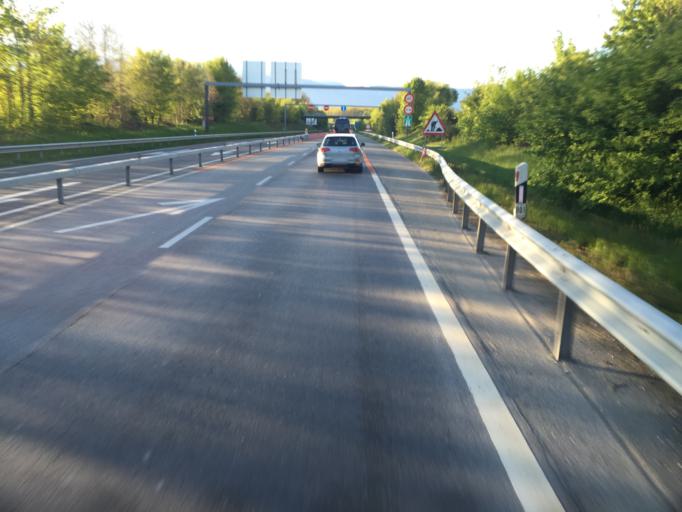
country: CH
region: Geneva
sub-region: Geneva
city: Confignon
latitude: 46.1793
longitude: 6.0843
